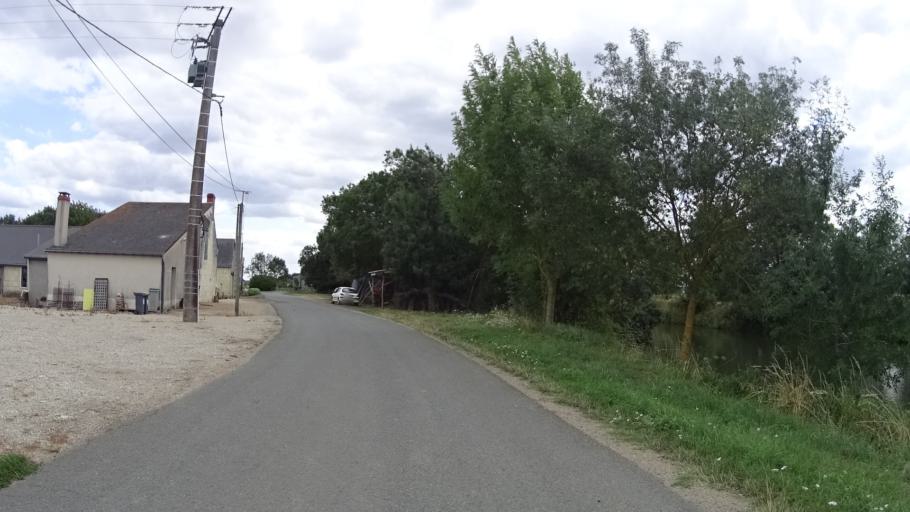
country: FR
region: Pays de la Loire
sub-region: Departement de Maine-et-Loire
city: Les Rosiers-sur-Loire
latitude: 47.3693
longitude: -0.1881
